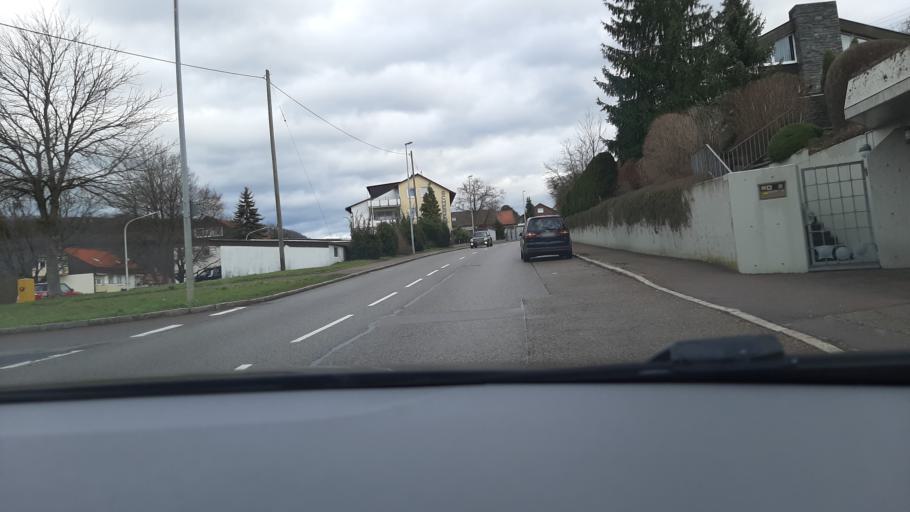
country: DE
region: Baden-Wuerttemberg
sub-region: Regierungsbezirk Stuttgart
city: Geislingen an der Steige
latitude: 48.6157
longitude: 9.8186
